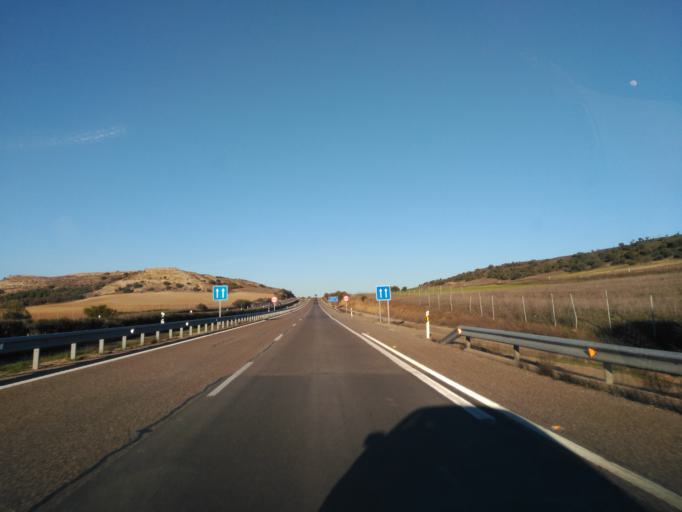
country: ES
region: Castille and Leon
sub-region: Provincia de Zamora
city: Castrillo de la Guarena
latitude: 41.1978
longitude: -5.3440
